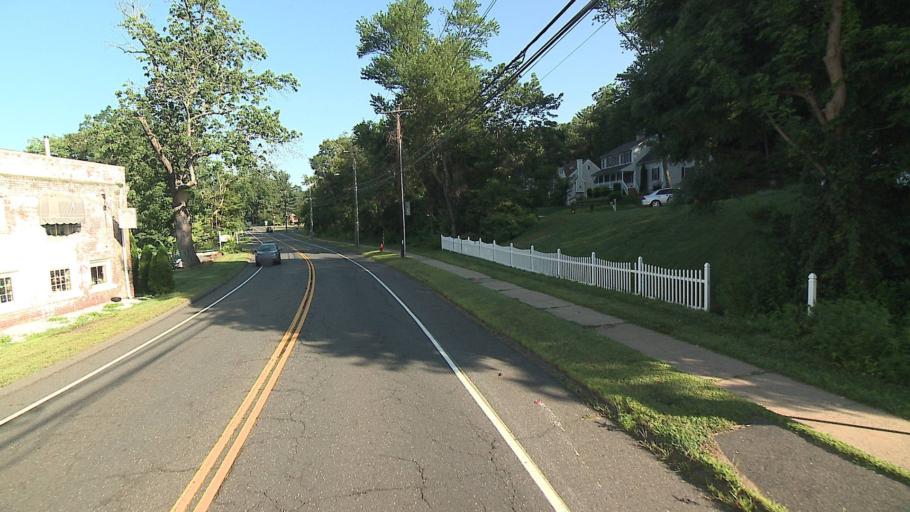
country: US
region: Connecticut
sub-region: Hartford County
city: Farmington
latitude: 41.7507
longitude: -72.8702
